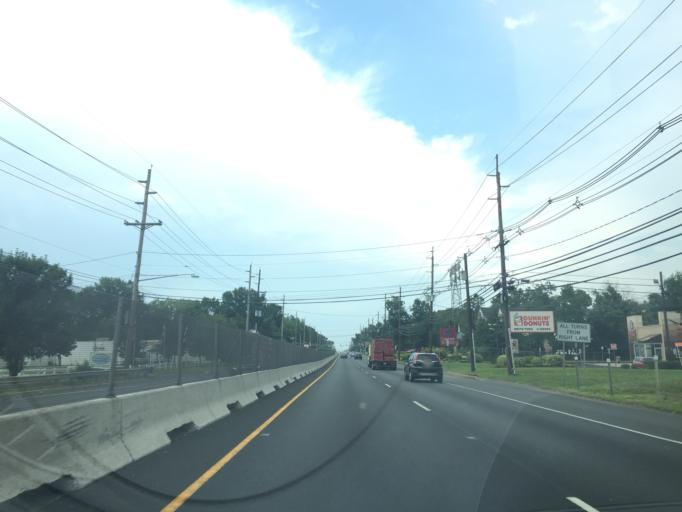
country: US
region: New Jersey
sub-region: Middlesex County
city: Kendall Park
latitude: 40.4293
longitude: -74.5189
